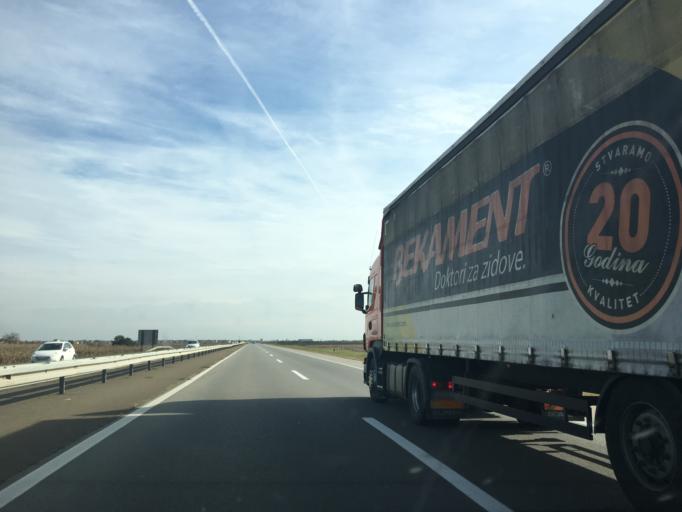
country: RS
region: Autonomna Pokrajina Vojvodina
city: Nova Pazova
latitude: 44.9636
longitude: 20.2450
